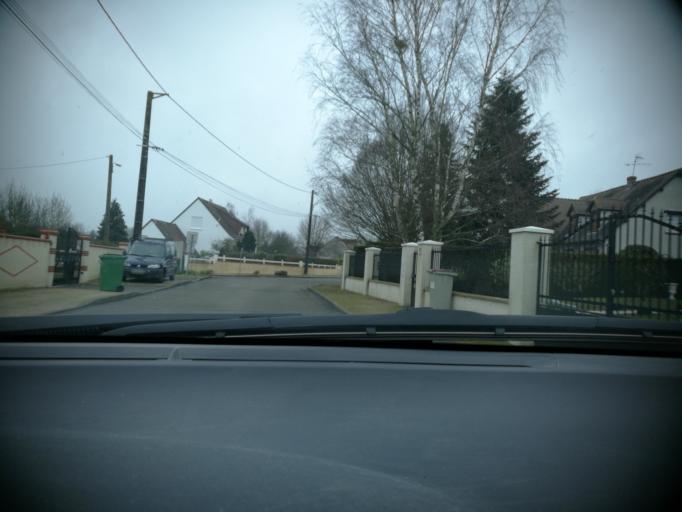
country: FR
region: Centre
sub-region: Departement du Loiret
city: Semoy
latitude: 47.9253
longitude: 1.9440
